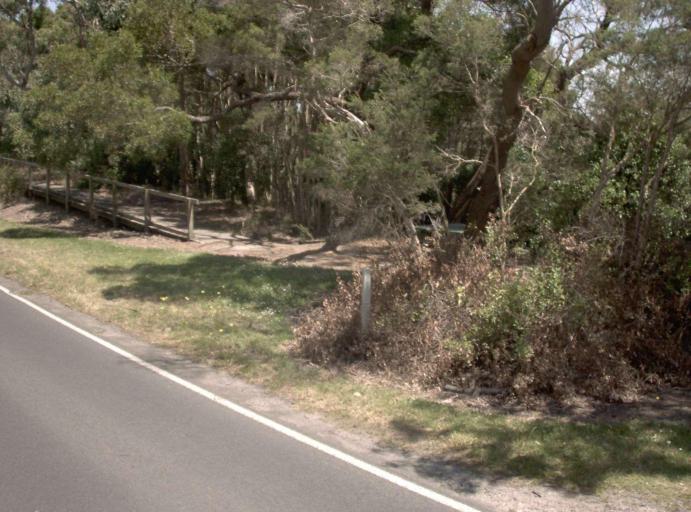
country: AU
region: Victoria
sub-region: Bass Coast
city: North Wonthaggi
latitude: -38.7019
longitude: 145.8723
